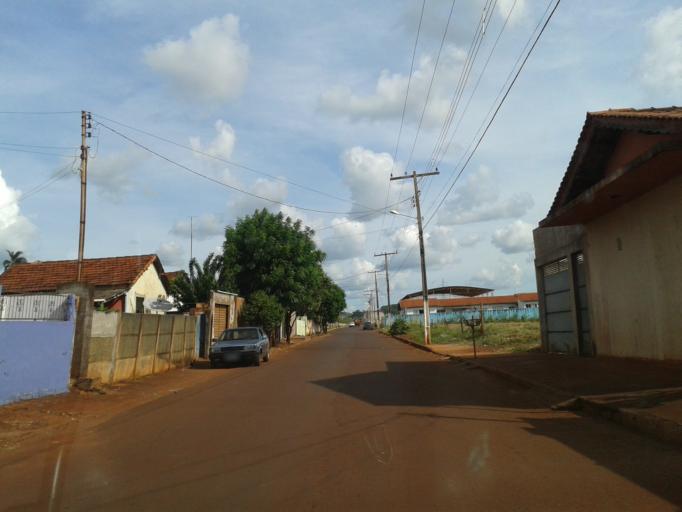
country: BR
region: Minas Gerais
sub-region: Centralina
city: Centralina
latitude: -18.5955
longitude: -49.1959
